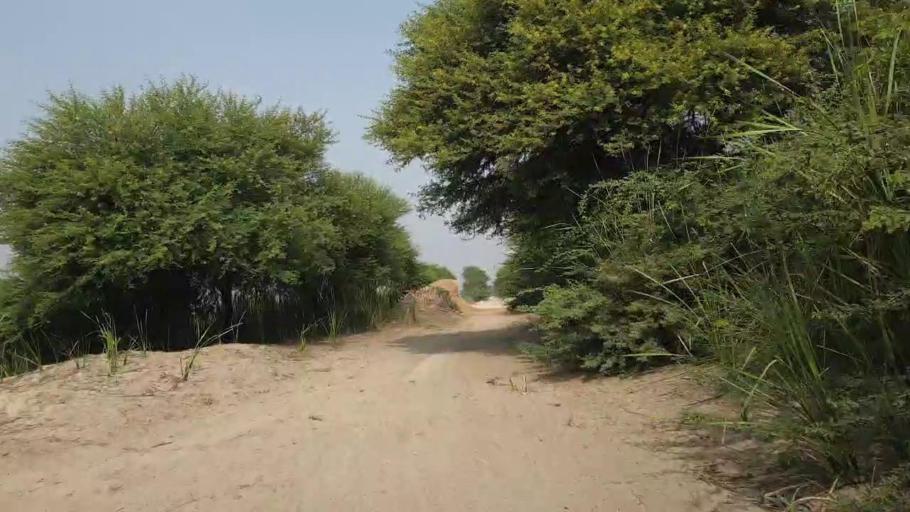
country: PK
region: Sindh
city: Kario
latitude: 24.7627
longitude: 68.5243
